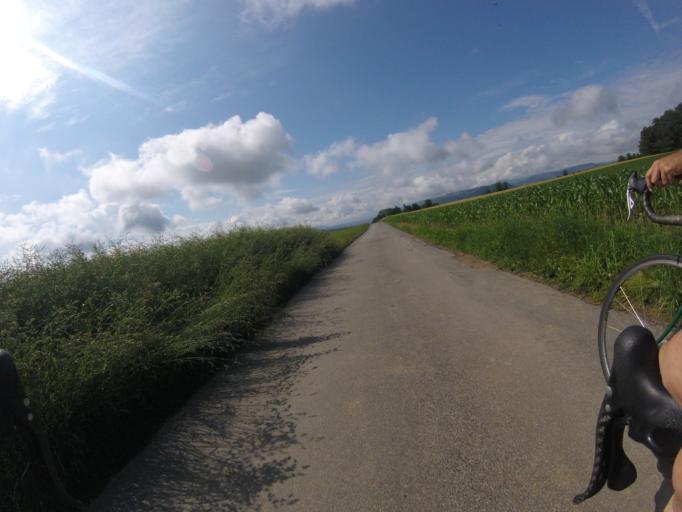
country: CH
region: Bern
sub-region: Bern-Mittelland District
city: Stettlen
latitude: 46.9391
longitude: 7.5382
